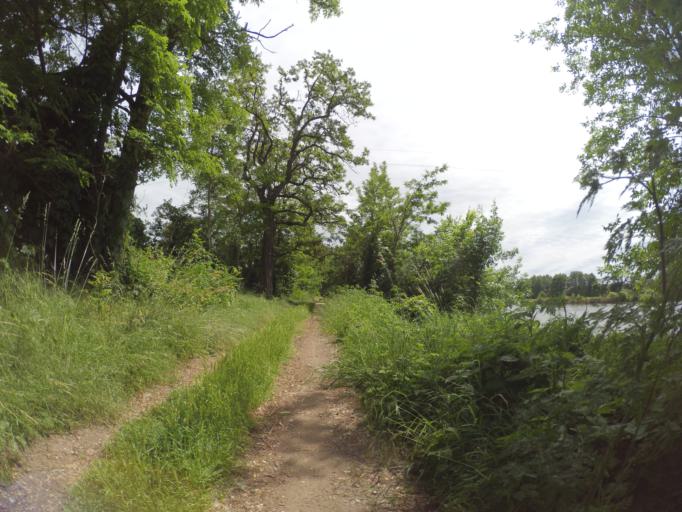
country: CZ
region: Central Bohemia
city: Lysa nad Labem
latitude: 50.1797
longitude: 14.8526
